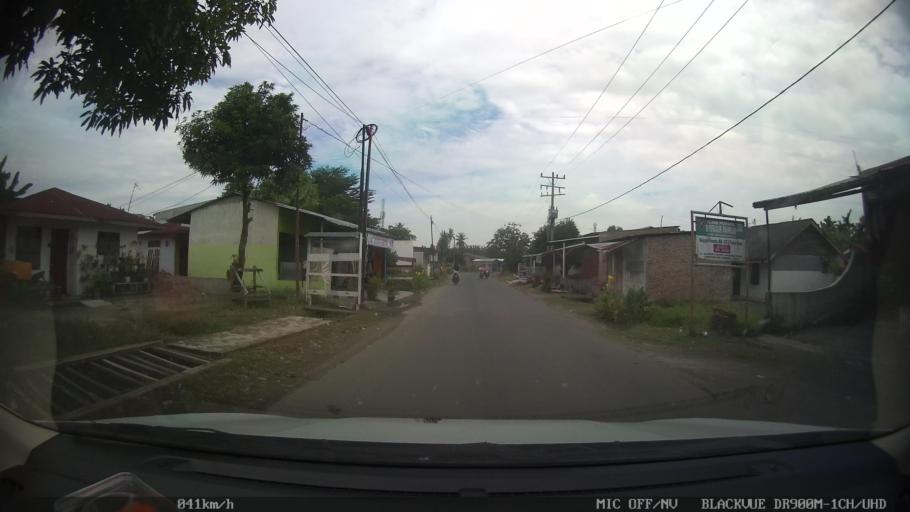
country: ID
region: North Sumatra
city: Sunggal
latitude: 3.6475
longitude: 98.5941
